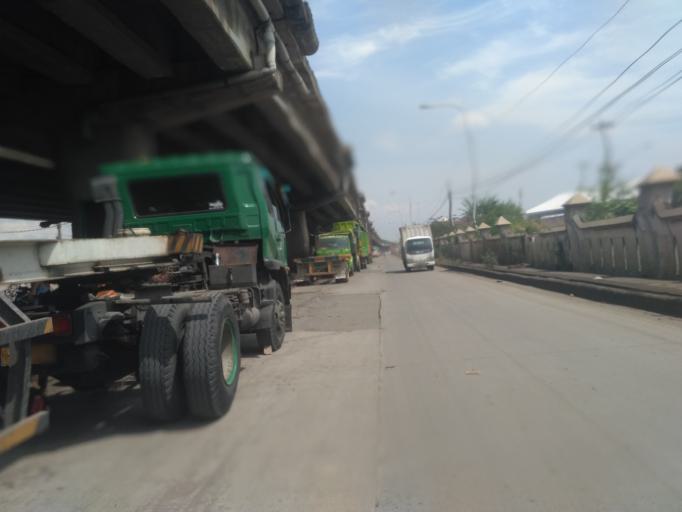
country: ID
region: Central Java
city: Semarang
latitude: -6.9555
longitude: 110.4273
